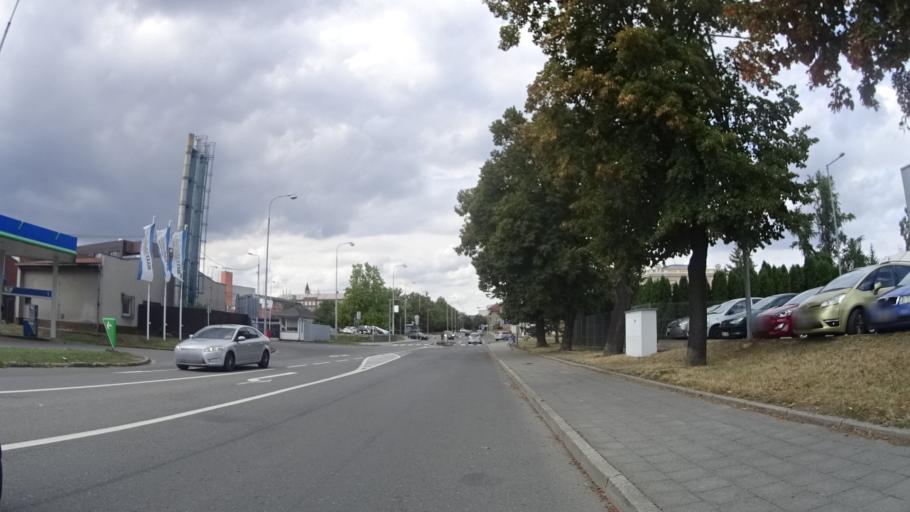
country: CZ
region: Olomoucky
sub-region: Okres Olomouc
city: Olomouc
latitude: 49.6021
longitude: 17.2437
